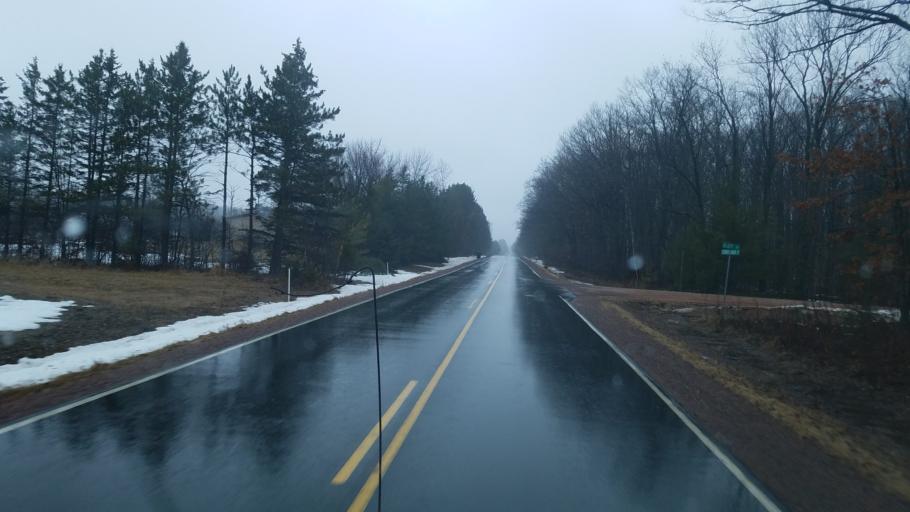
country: US
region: Wisconsin
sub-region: Wood County
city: Marshfield
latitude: 44.5266
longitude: -90.2995
